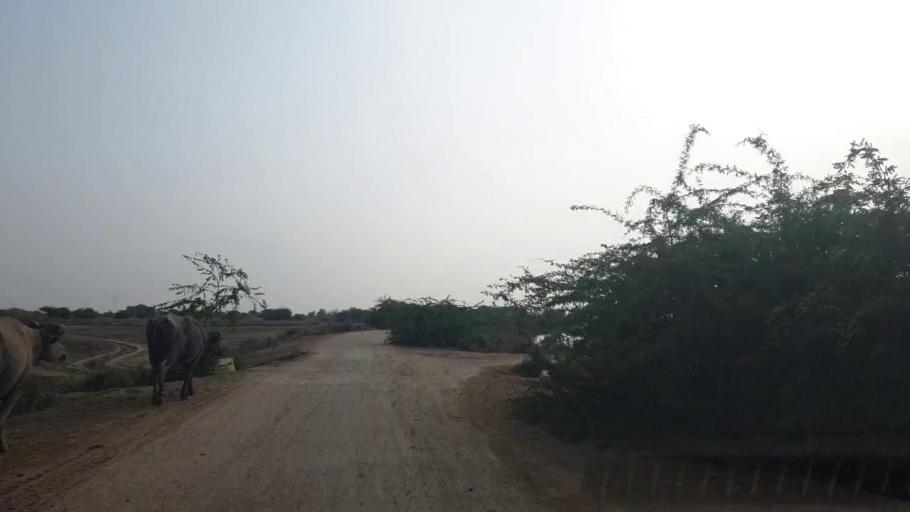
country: PK
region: Sindh
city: Badin
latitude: 24.6292
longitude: 68.6921
